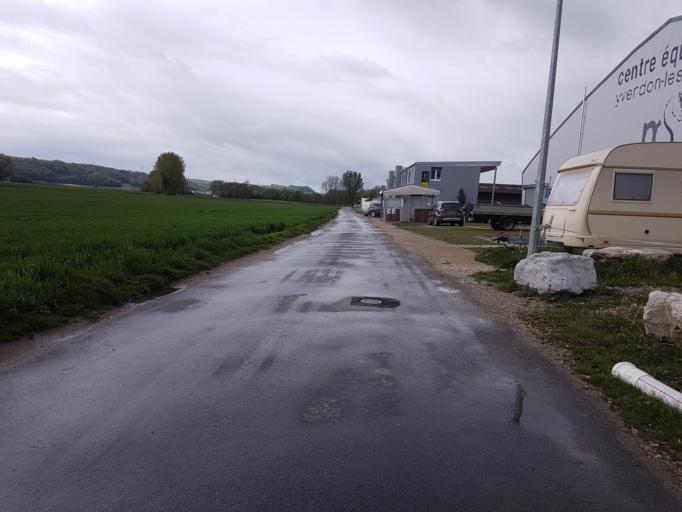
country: CH
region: Vaud
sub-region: Jura-Nord vaudois District
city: Yverdon-les-Bains
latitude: 46.7700
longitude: 6.6269
